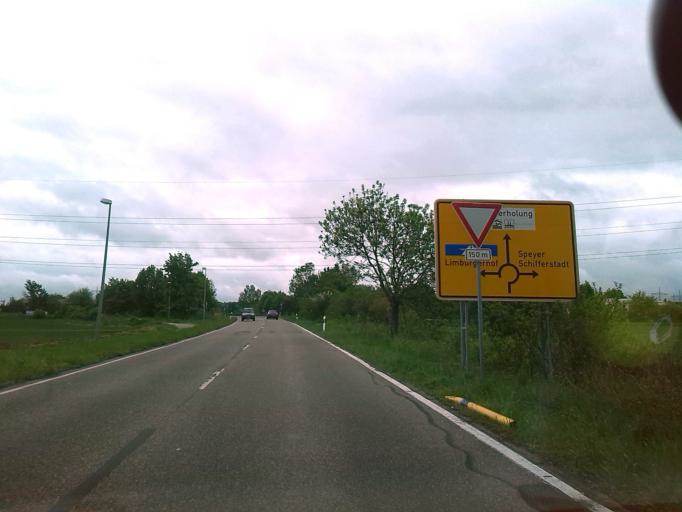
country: DE
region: Rheinland-Pfalz
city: Mutterstadt
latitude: 49.4307
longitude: 8.3616
